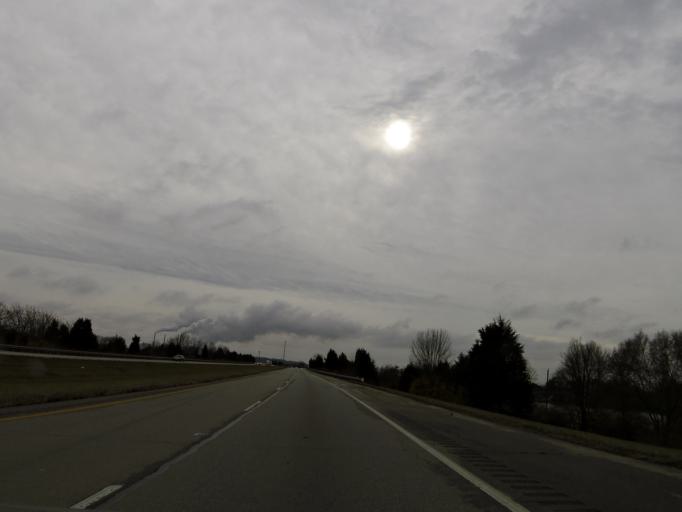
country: US
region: Indiana
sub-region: Dearborn County
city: Hidden Valley
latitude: 39.1545
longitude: -84.8170
